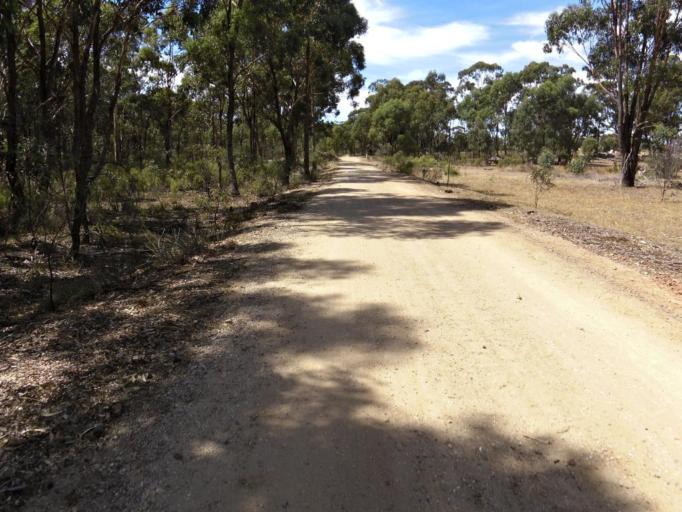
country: AU
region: Victoria
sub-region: Greater Bendigo
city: White Hills
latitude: -36.7551
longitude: 144.3272
